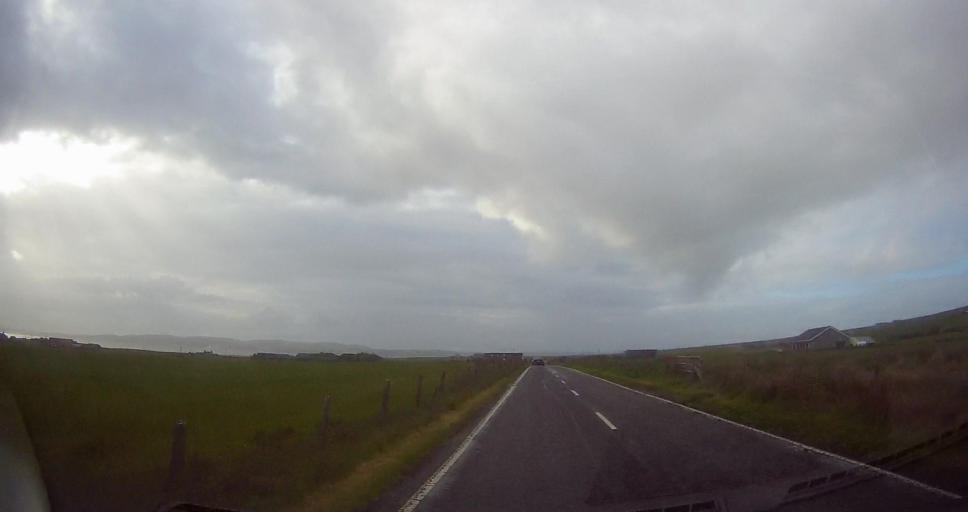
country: GB
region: Scotland
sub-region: Orkney Islands
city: Stromness
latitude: 58.9344
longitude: -3.2105
